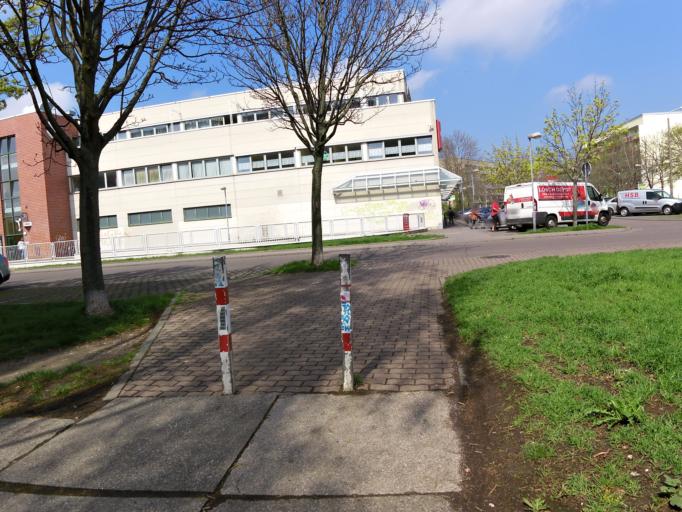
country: DE
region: Saxony
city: Markranstadt
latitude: 51.3214
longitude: 12.2720
